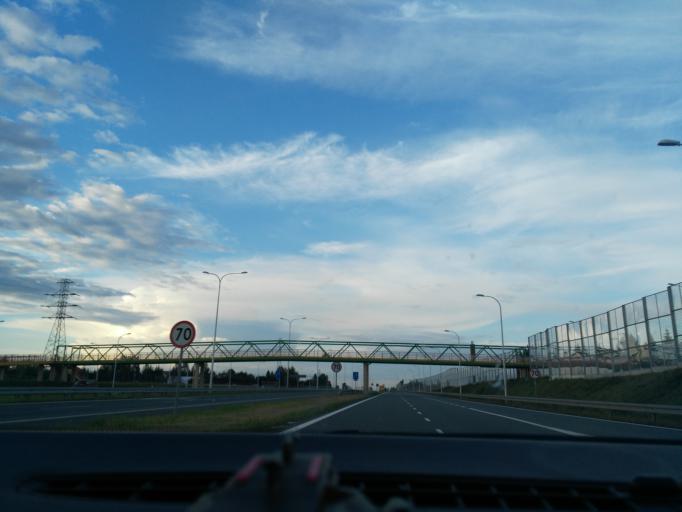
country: PL
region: Lublin Voivodeship
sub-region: Powiat lubelski
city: Jakubowice Murowane
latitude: 51.3041
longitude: 22.5900
